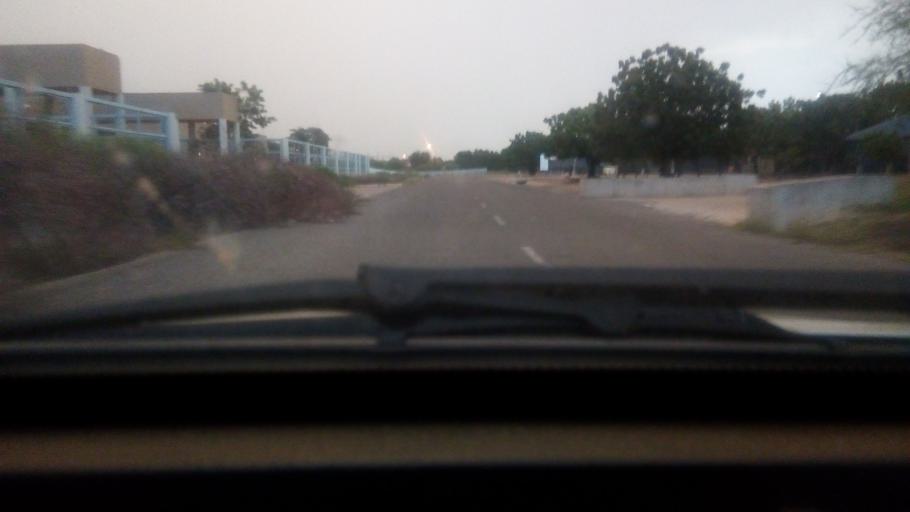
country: BW
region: Kweneng
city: Mmopone
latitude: -24.5906
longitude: 25.9162
